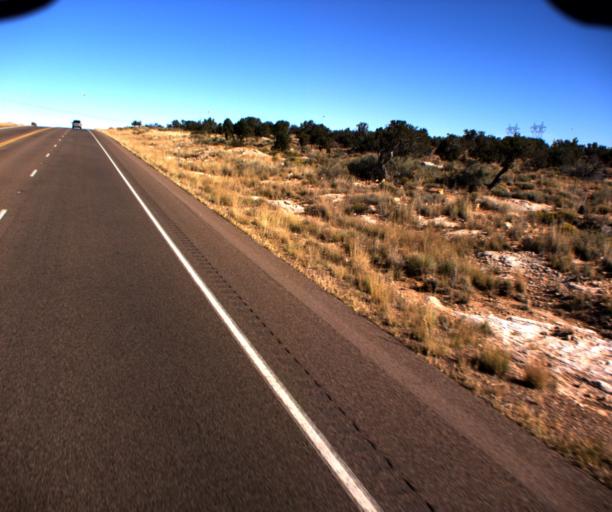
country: US
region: Arizona
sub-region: Navajo County
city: Snowflake
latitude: 34.6286
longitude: -110.0937
